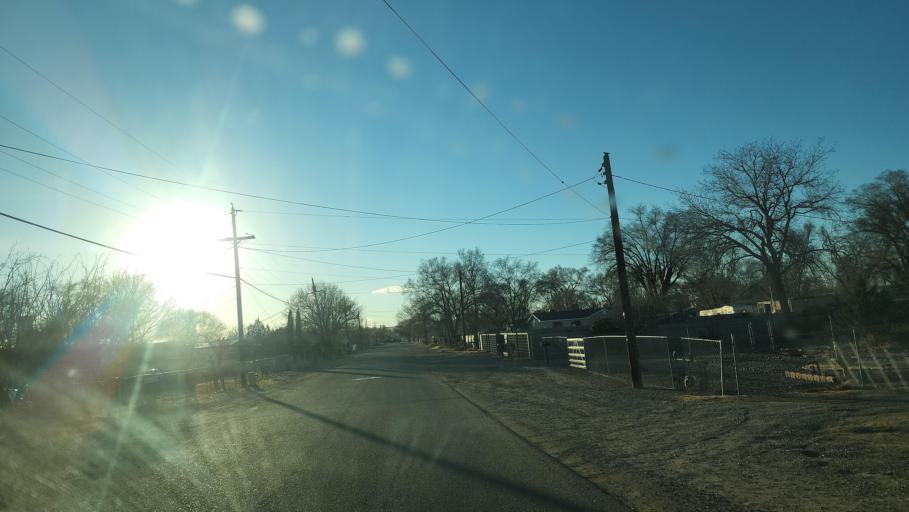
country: US
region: New Mexico
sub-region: Bernalillo County
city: South Valley
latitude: 35.0307
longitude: -106.6759
